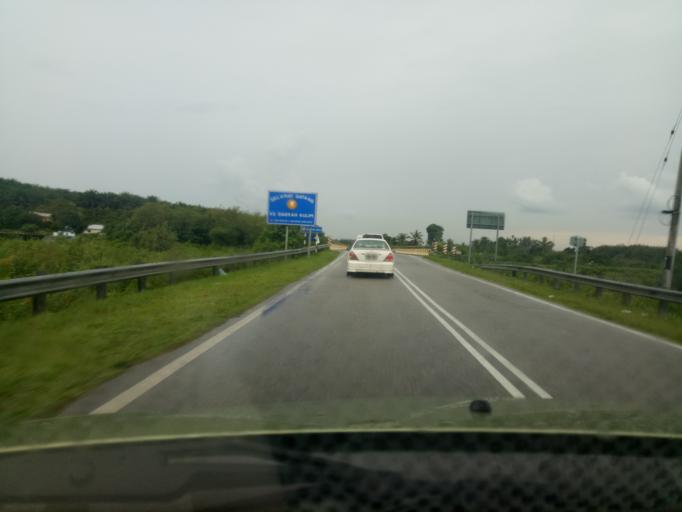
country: MY
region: Penang
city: Tasek Glugor
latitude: 5.5221
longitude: 100.5771
